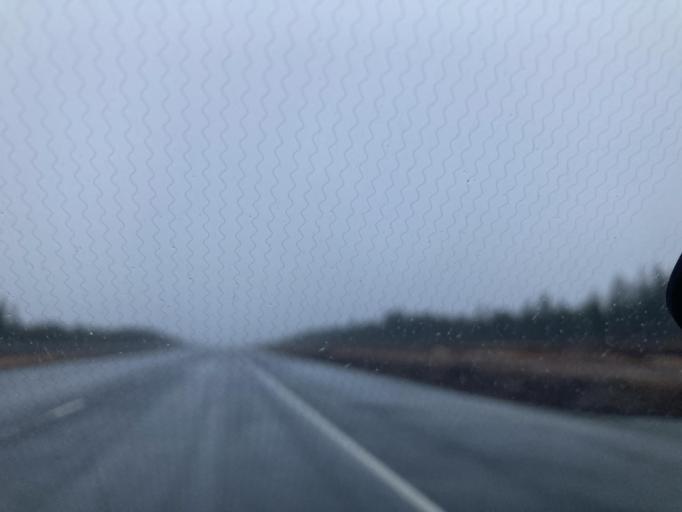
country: FI
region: Lapland
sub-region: Rovaniemi
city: Rovaniemi
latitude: 66.5781
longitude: 25.7993
